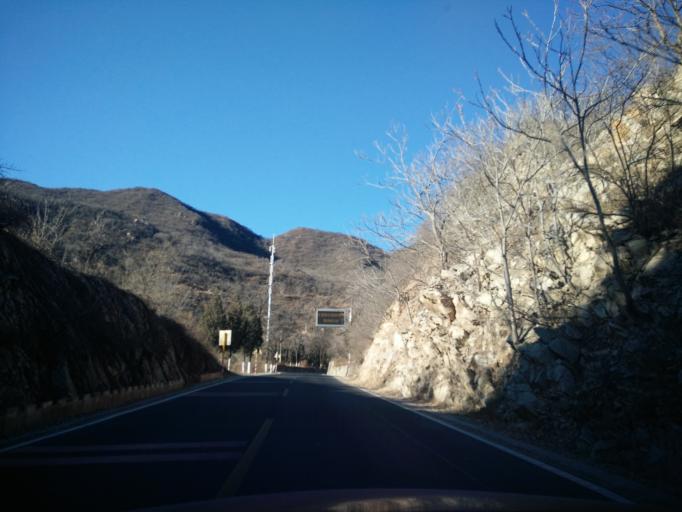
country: CN
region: Beijing
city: Wangping
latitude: 40.0073
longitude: 115.9684
